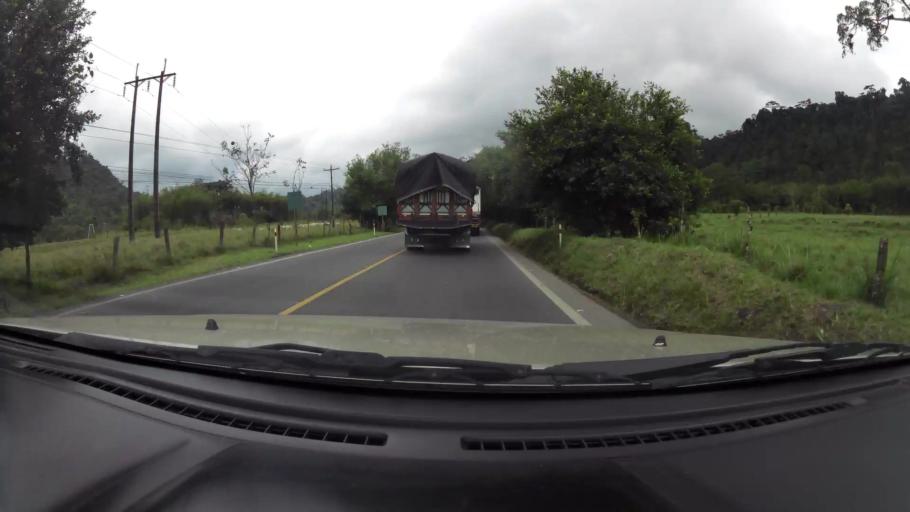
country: EC
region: Santo Domingo de los Tsachilas
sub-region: Canton Santo Domingo de los Colorados
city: Santo Domingo de los Colorados
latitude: -0.2888
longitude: -79.0651
